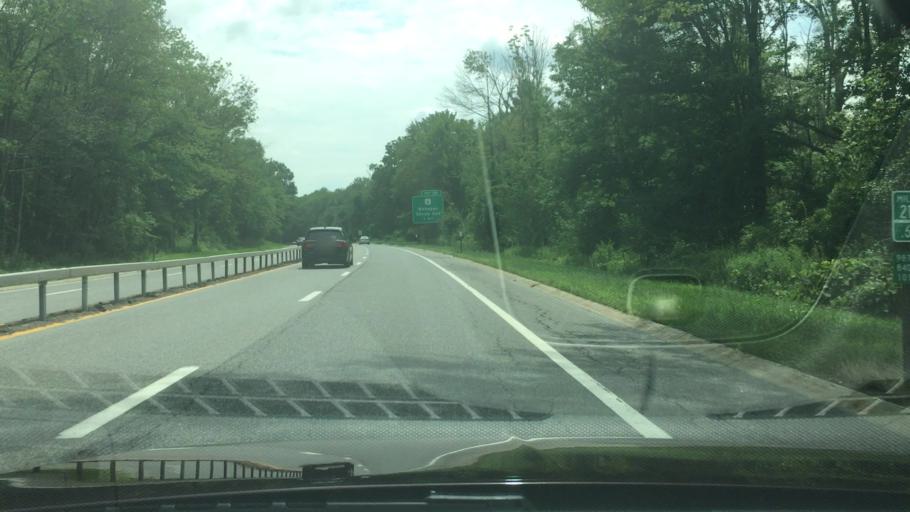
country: US
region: New York
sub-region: Westchester County
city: Shrub Oak
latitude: 41.3520
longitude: -73.8106
